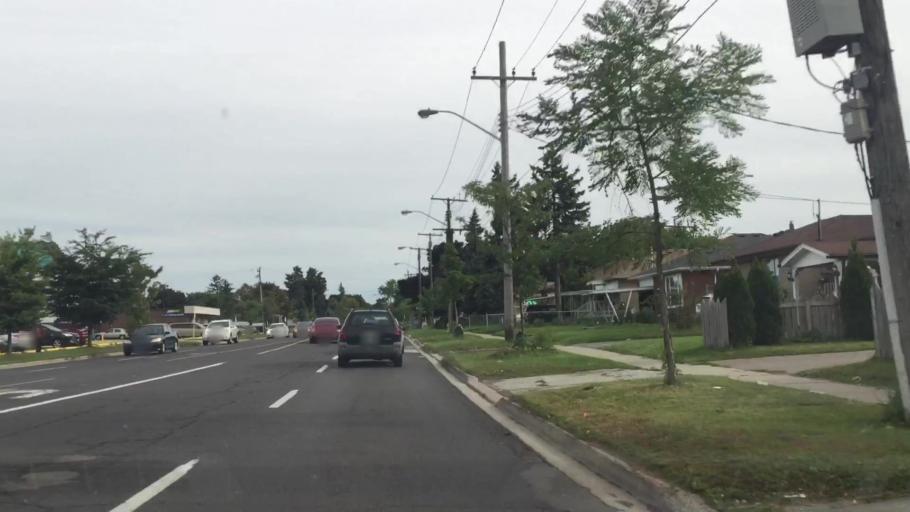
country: CA
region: Ontario
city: Scarborough
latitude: 43.7545
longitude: -79.2452
